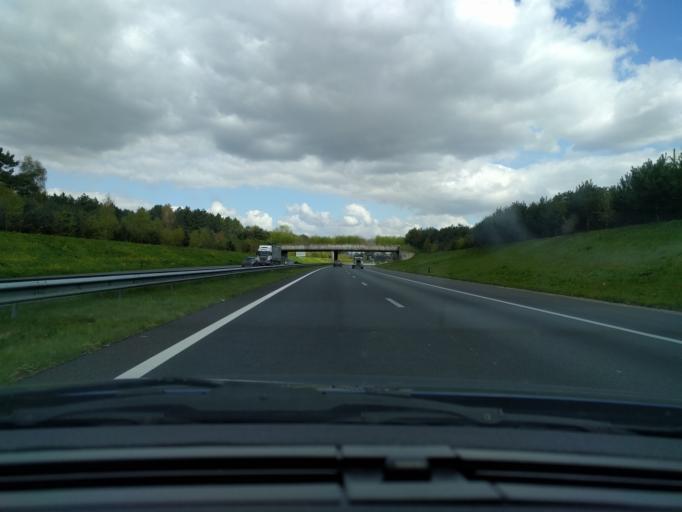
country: NL
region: North Brabant
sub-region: Gemeente Son en Breugel
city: Son
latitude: 51.5197
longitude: 5.4683
